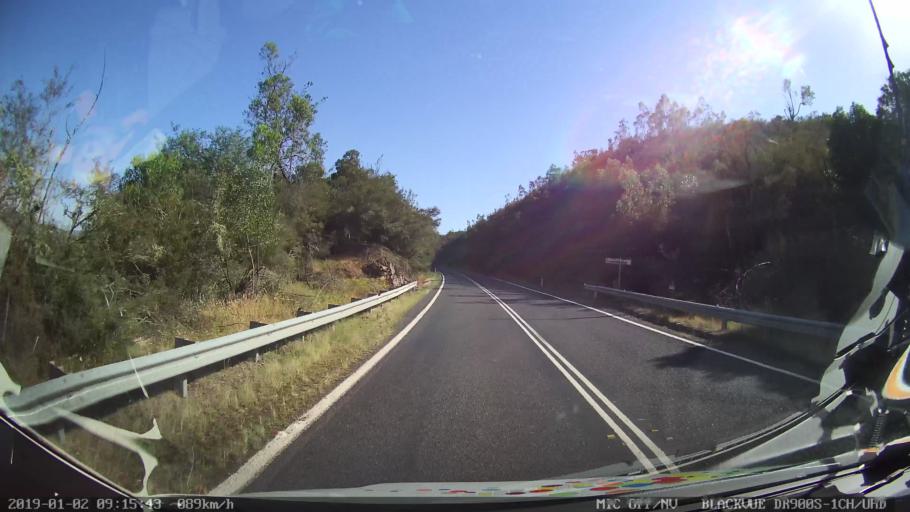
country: AU
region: New South Wales
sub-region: Tumut Shire
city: Tumut
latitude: -35.4619
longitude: 148.2815
